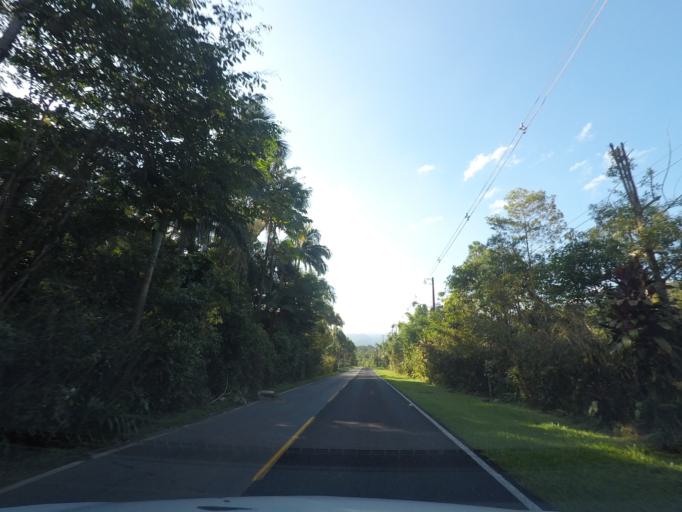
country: BR
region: Parana
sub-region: Antonina
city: Antonina
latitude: -25.4132
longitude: -48.8735
